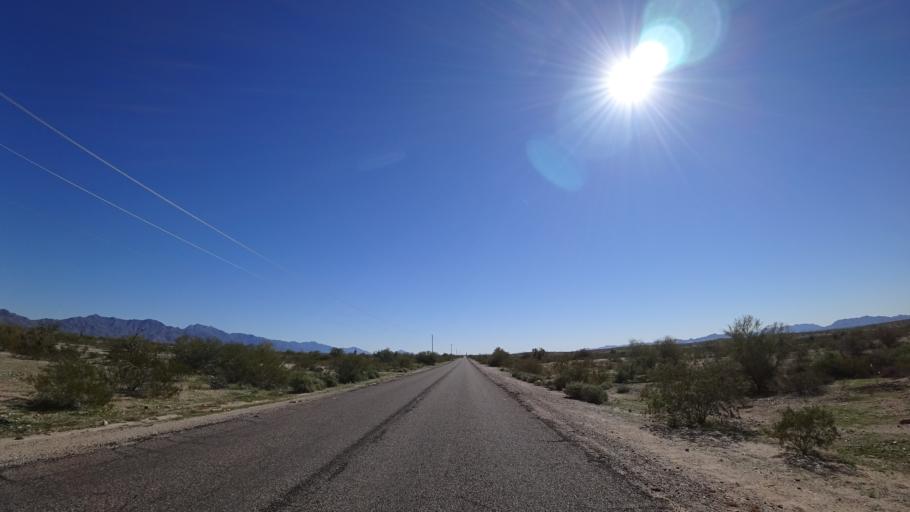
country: US
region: Arizona
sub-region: Maricopa County
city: Buckeye
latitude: 33.3070
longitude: -112.4630
